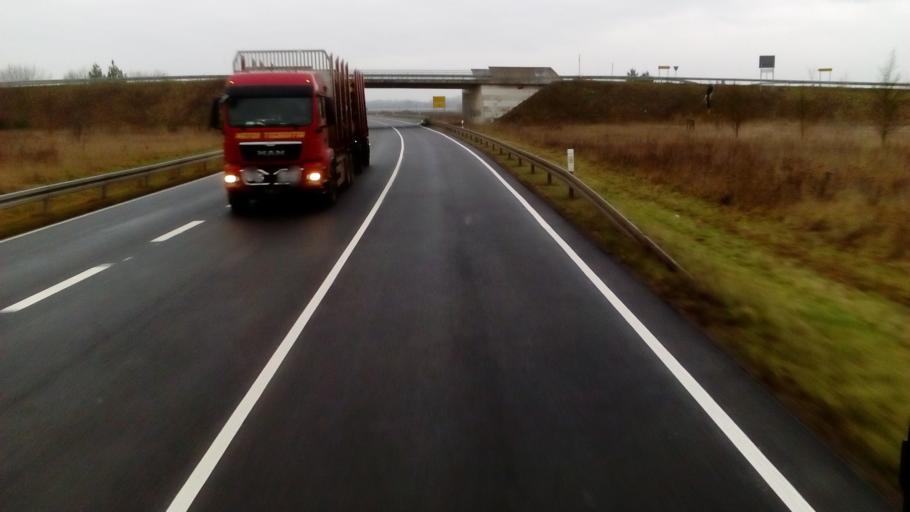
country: DE
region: Brandenburg
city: Perleberg
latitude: 53.0607
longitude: 11.8330
